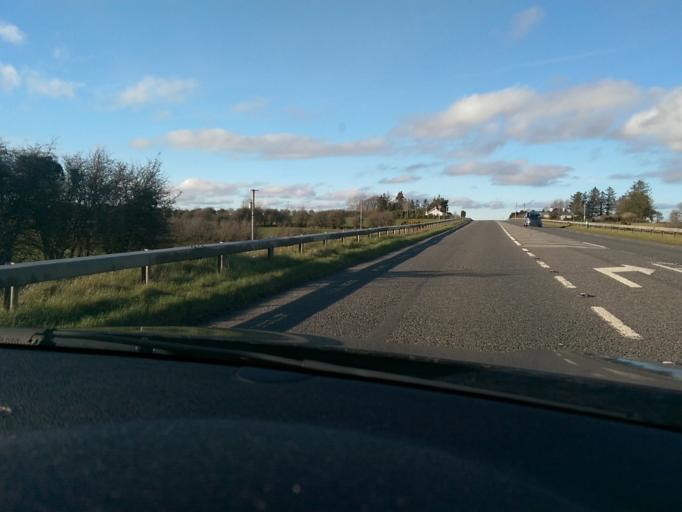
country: IE
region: Connaught
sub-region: Roscommon
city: Roscommon
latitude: 53.6664
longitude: -8.1981
